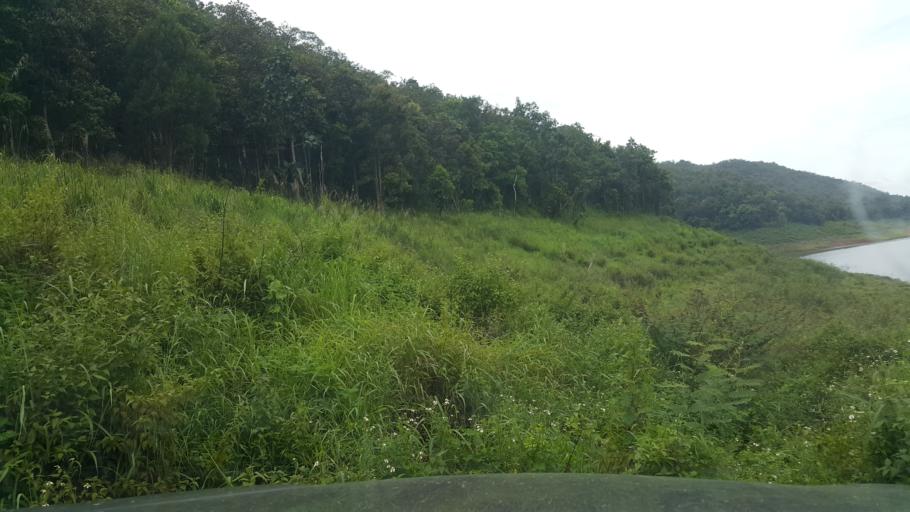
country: TH
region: Chiang Mai
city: San Sai
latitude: 18.9628
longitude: 99.1238
